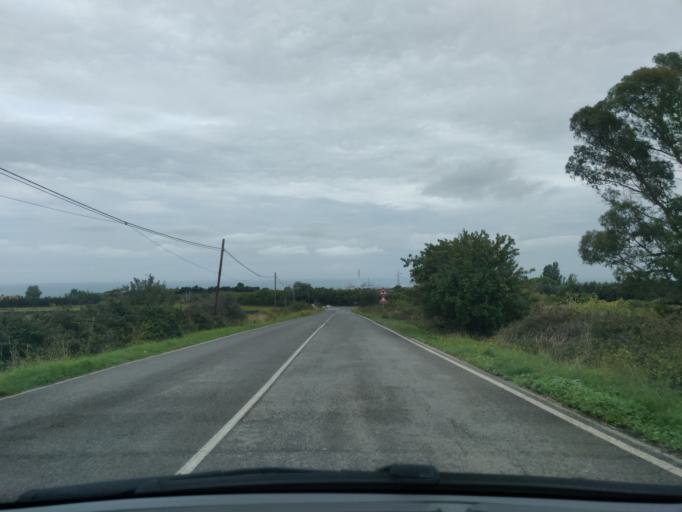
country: IT
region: Latium
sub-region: Citta metropolitana di Roma Capitale
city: Civitavecchia
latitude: 42.1074
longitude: 11.8357
